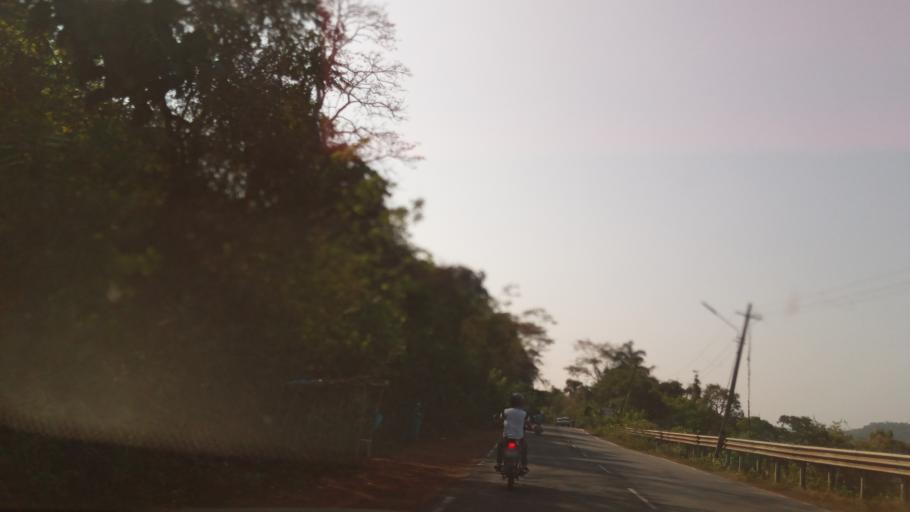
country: IN
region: Goa
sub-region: North Goa
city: Bandora
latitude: 15.4342
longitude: 73.9851
